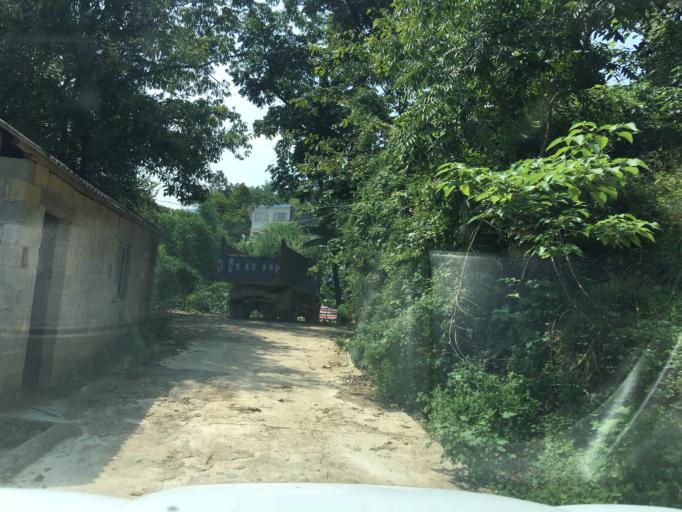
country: CN
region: Guangxi Zhuangzu Zizhiqu
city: Xinzhou
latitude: 24.9952
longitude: 105.7554
